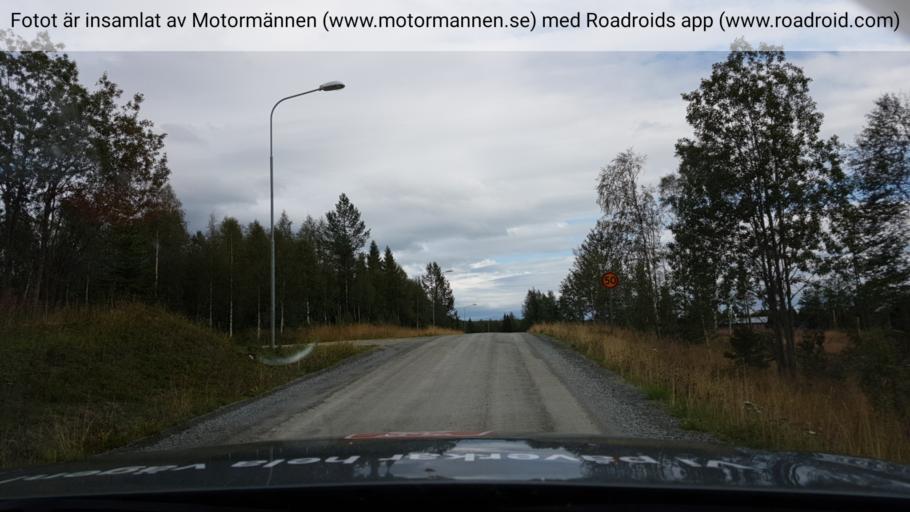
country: SE
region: Jaemtland
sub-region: Krokoms Kommun
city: Valla
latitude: 63.6937
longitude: 13.6585
